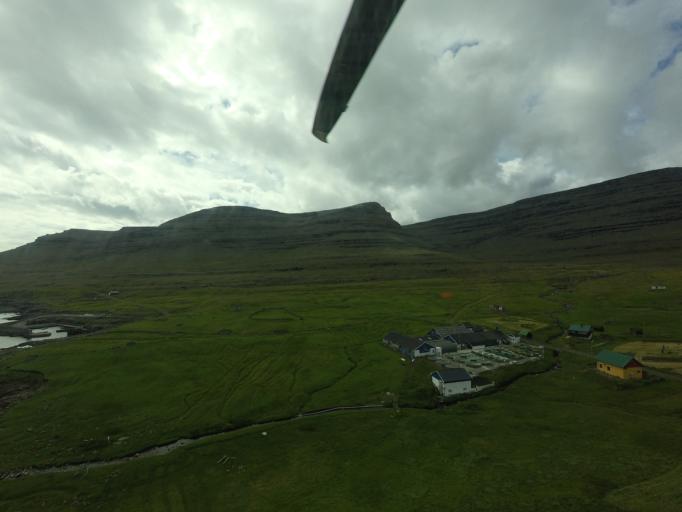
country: FO
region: Nordoyar
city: Klaksvik
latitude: 62.2771
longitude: -6.3409
